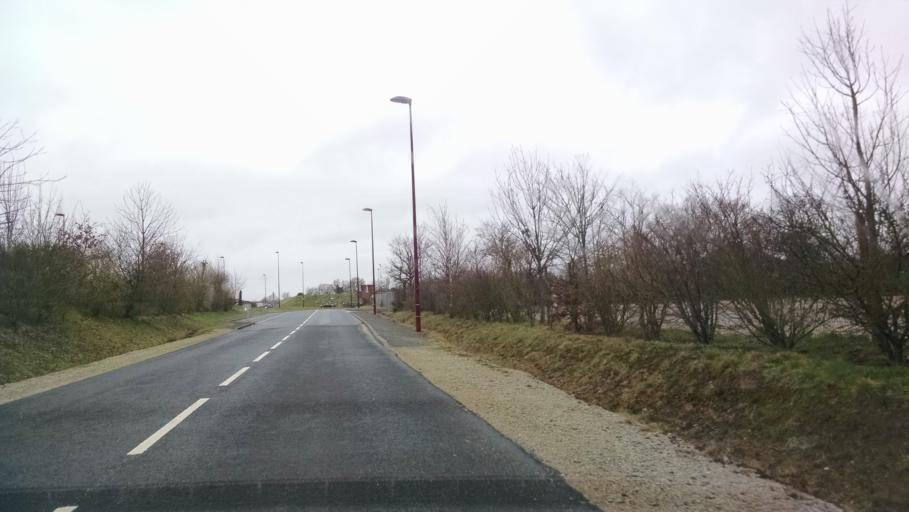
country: FR
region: Pays de la Loire
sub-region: Departement de la Loire-Atlantique
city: Clisson
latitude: 47.0963
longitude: -1.2696
